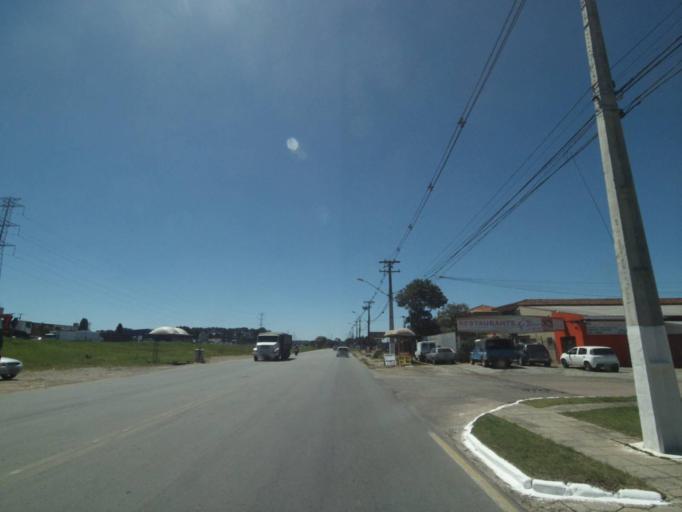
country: BR
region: Parana
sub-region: Curitiba
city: Curitiba
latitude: -25.4800
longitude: -49.3490
